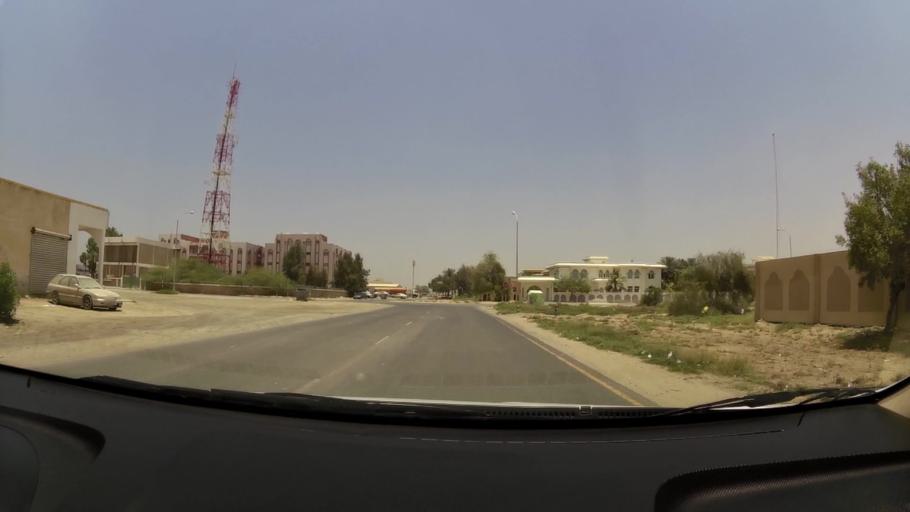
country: AE
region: Umm al Qaywayn
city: Umm al Qaywayn
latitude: 25.5374
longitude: 55.5410
